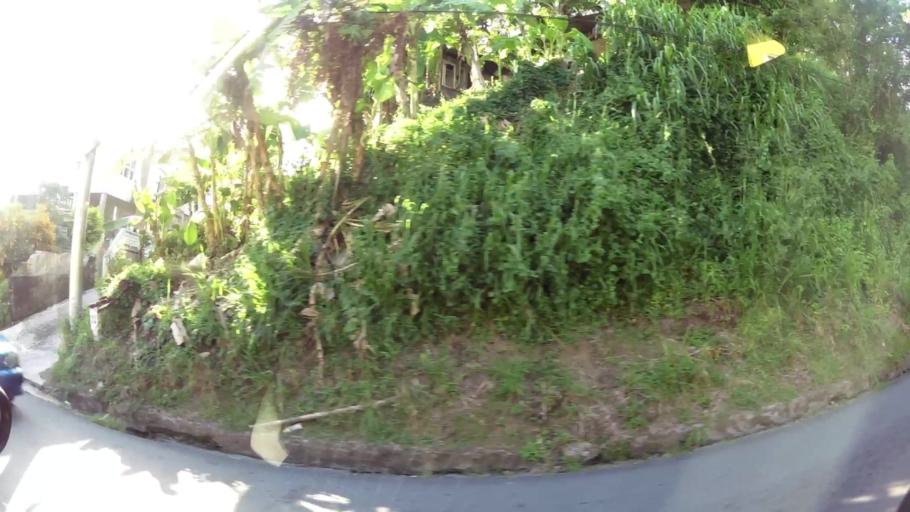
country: TT
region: Eastern Tobago
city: Roxborough
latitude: 11.2223
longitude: -60.6132
